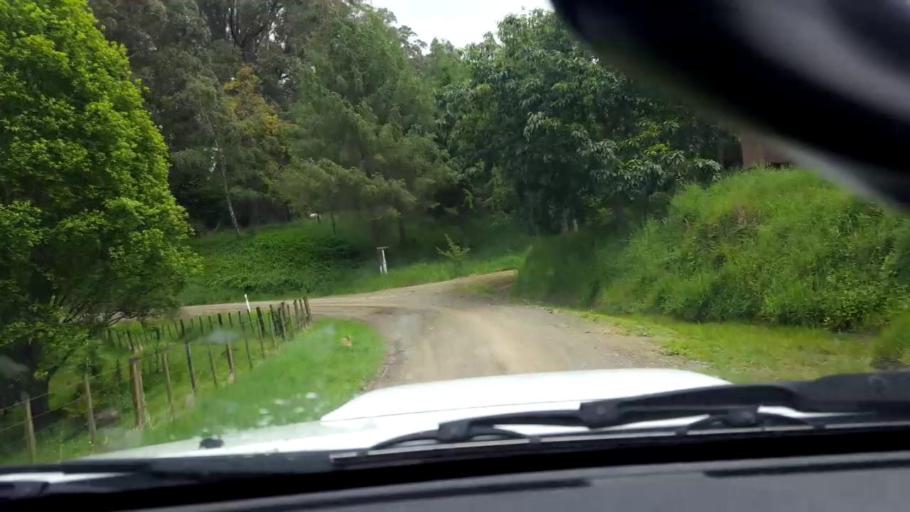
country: NZ
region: Gisborne
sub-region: Gisborne District
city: Gisborne
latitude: -38.3850
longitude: 177.6312
